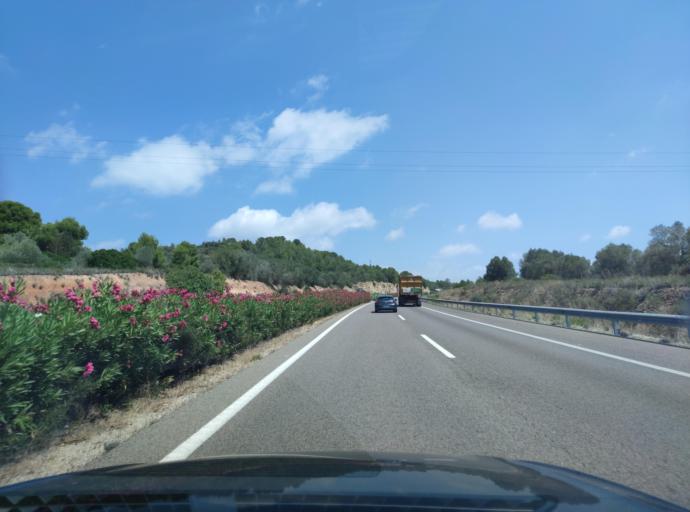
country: ES
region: Catalonia
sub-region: Provincia de Tarragona
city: Masdenverge
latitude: 40.6720
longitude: 0.5155
